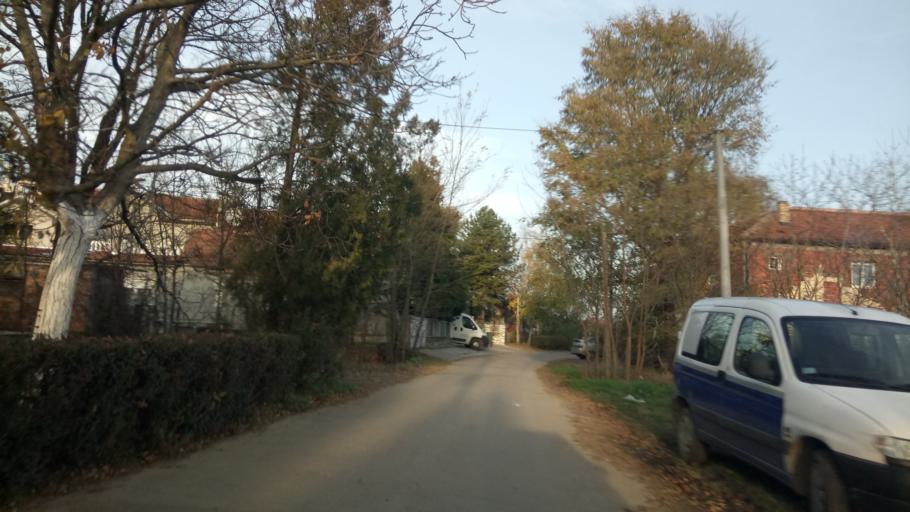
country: RS
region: Autonomna Pokrajina Vojvodina
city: Nova Pazova
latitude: 44.9385
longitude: 20.2175
